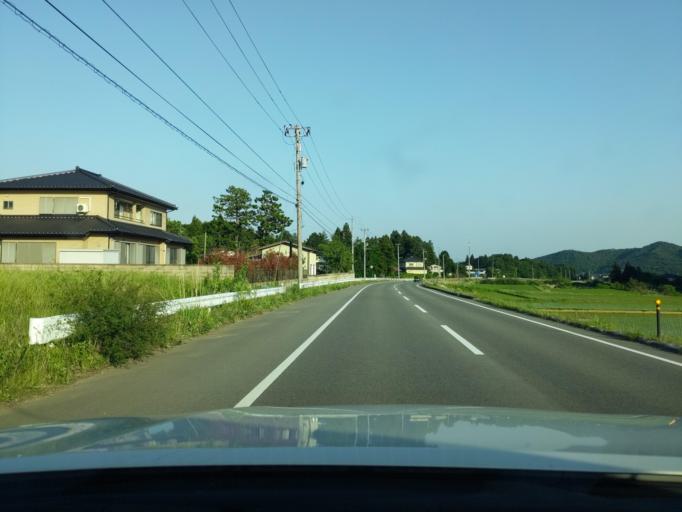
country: JP
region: Fukushima
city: Motomiya
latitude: 37.5352
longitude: 140.3607
